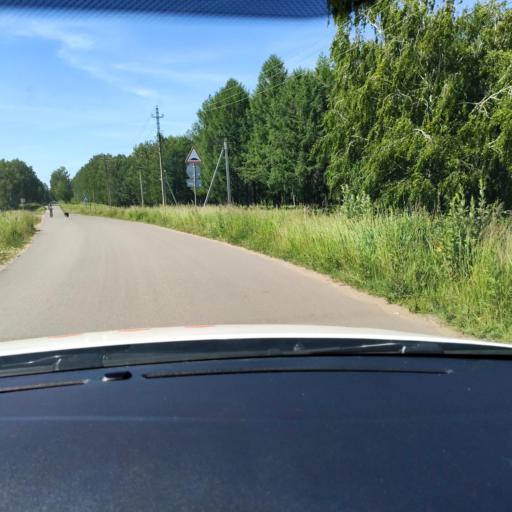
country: RU
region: Tatarstan
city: Staroye Arakchino
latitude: 55.8859
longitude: 49.0391
